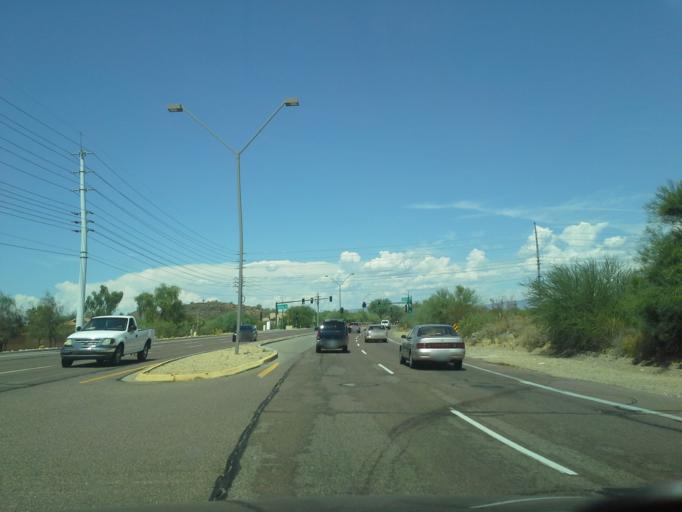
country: US
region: Arizona
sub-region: Maricopa County
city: Cave Creek
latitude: 33.6899
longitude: -112.0311
